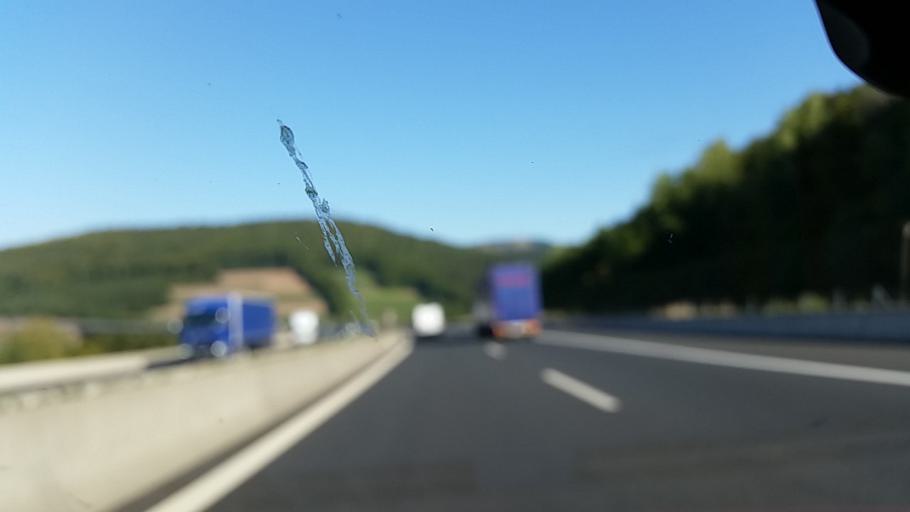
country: DE
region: Bavaria
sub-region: Regierungsbezirk Unterfranken
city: Riedenberg
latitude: 50.3108
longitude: 9.8482
